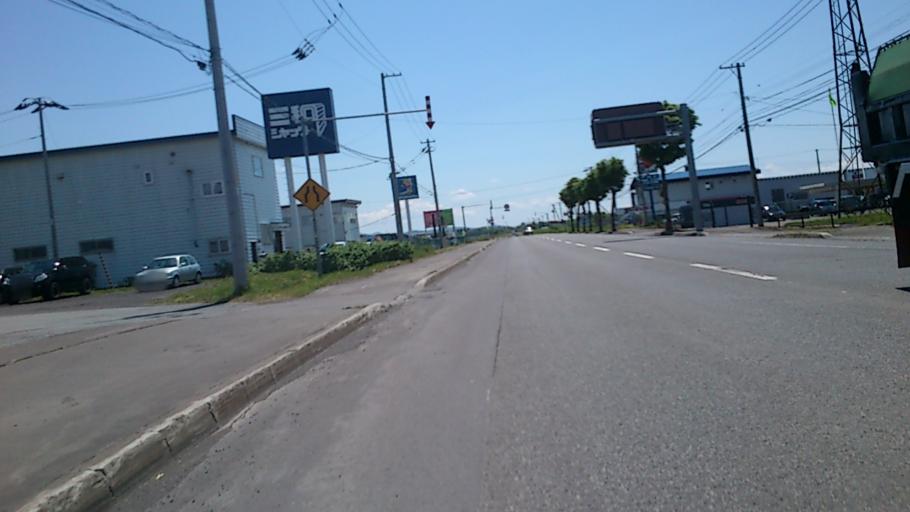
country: JP
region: Hokkaido
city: Nayoro
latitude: 44.3231
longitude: 142.4574
